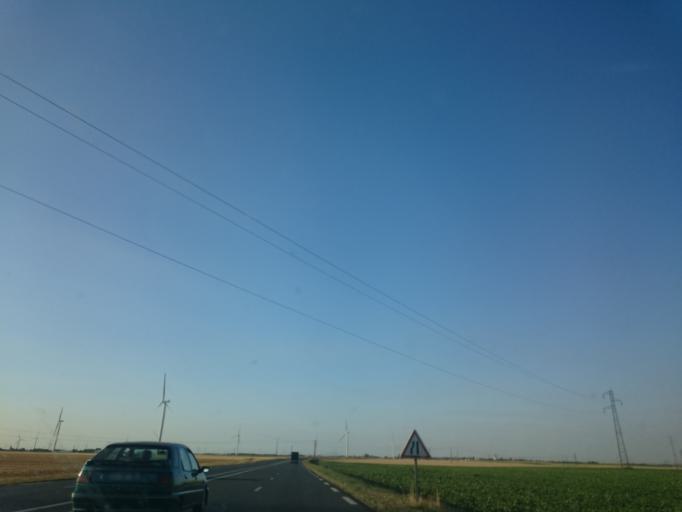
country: FR
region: Centre
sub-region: Departement d'Eure-et-Loir
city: Toury
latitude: 48.1539
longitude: 1.9090
